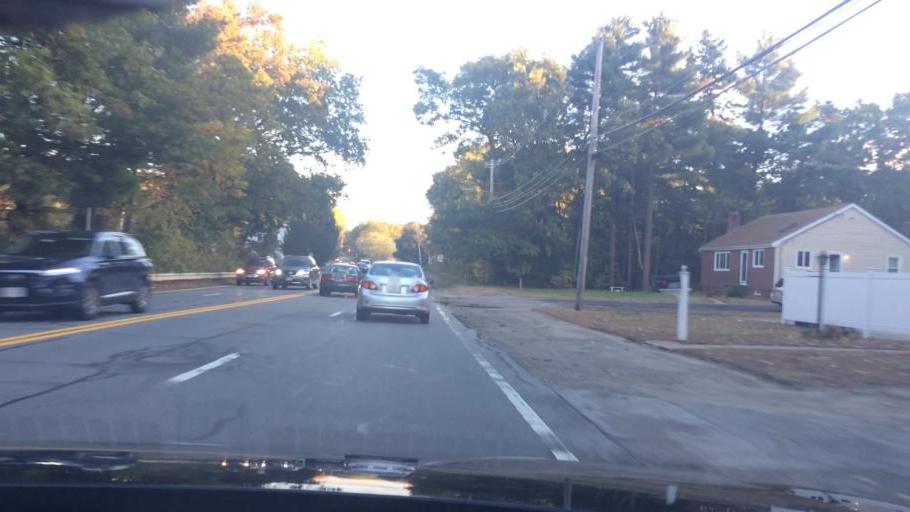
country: US
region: Massachusetts
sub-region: Middlesex County
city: Chelmsford
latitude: 42.6302
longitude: -71.3730
